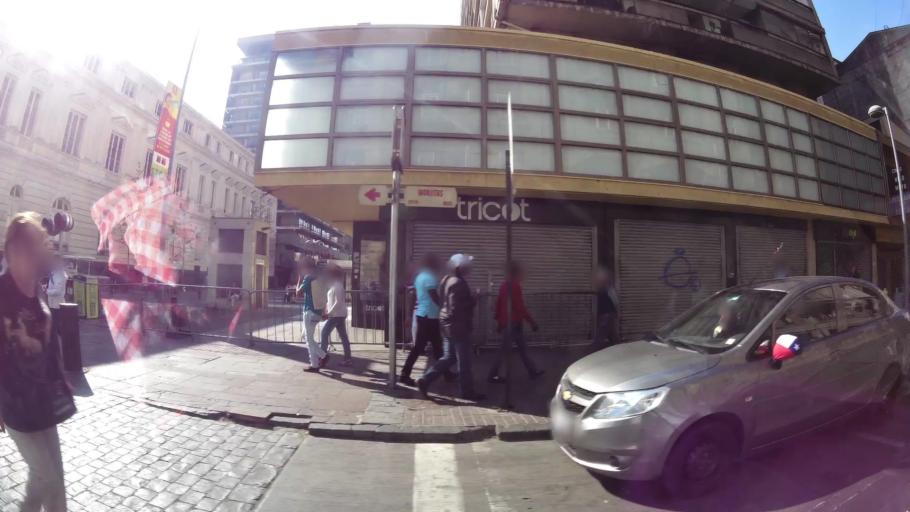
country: CL
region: Santiago Metropolitan
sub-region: Provincia de Santiago
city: Santiago
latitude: -33.4373
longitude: -70.6496
